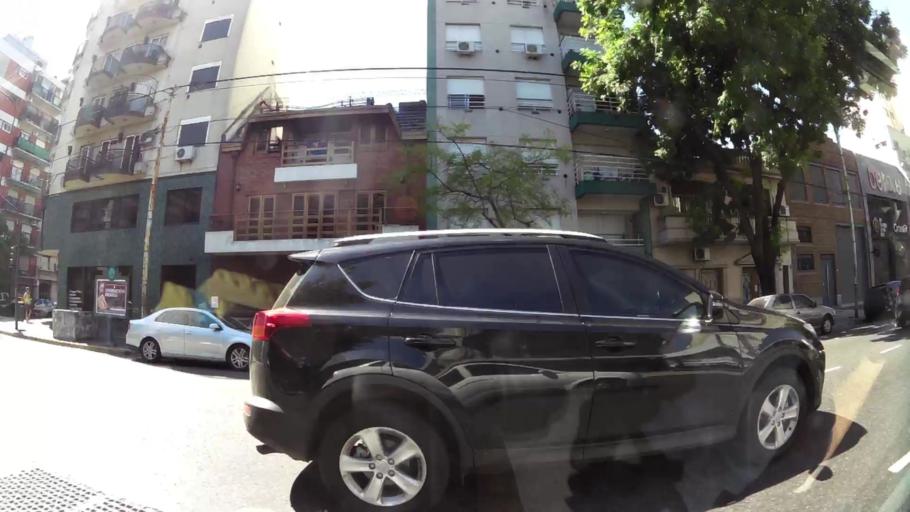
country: AR
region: Buenos Aires F.D.
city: Villa Santa Rita
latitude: -34.6275
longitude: -58.4306
